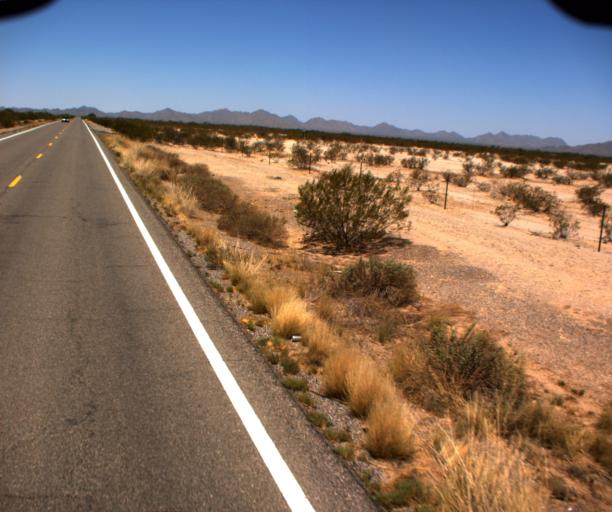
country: US
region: Arizona
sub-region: Pinal County
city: Maricopa
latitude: 33.0410
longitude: -112.3287
